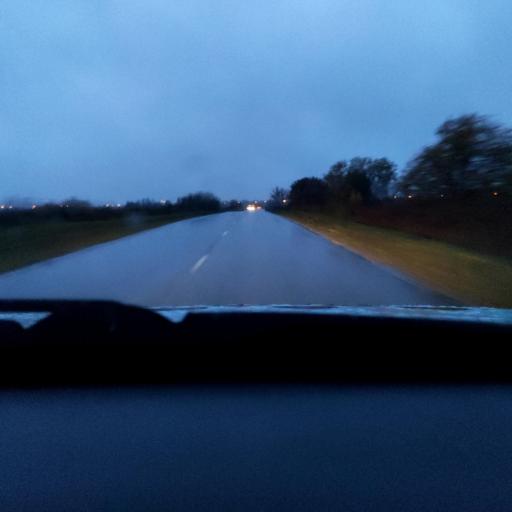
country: RU
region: Perm
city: Kondratovo
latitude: 57.9939
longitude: 56.0891
